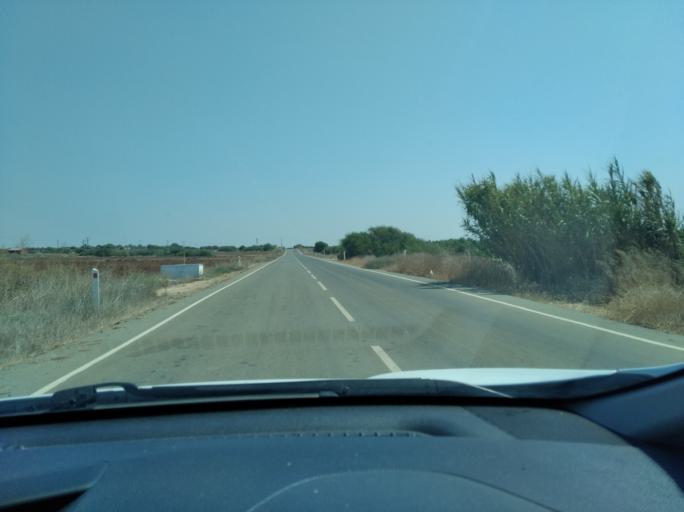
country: CY
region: Larnaka
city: Xylotymbou
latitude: 34.9859
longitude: 33.7529
